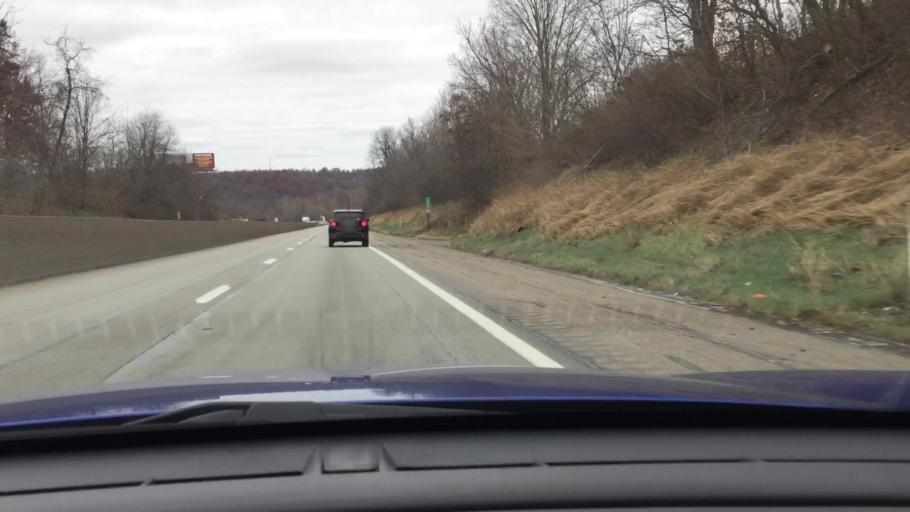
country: US
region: Pennsylvania
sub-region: Westmoreland County
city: New Stanton
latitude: 40.2049
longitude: -79.6794
